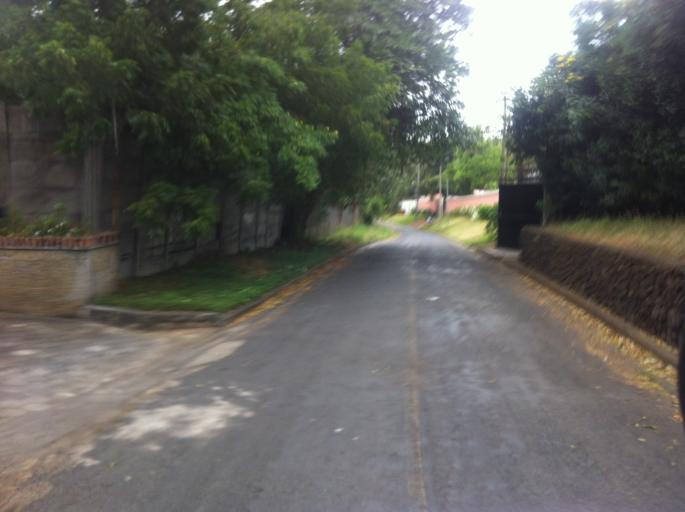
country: NI
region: Managua
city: Ciudad Sandino
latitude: 12.0810
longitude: -86.3229
